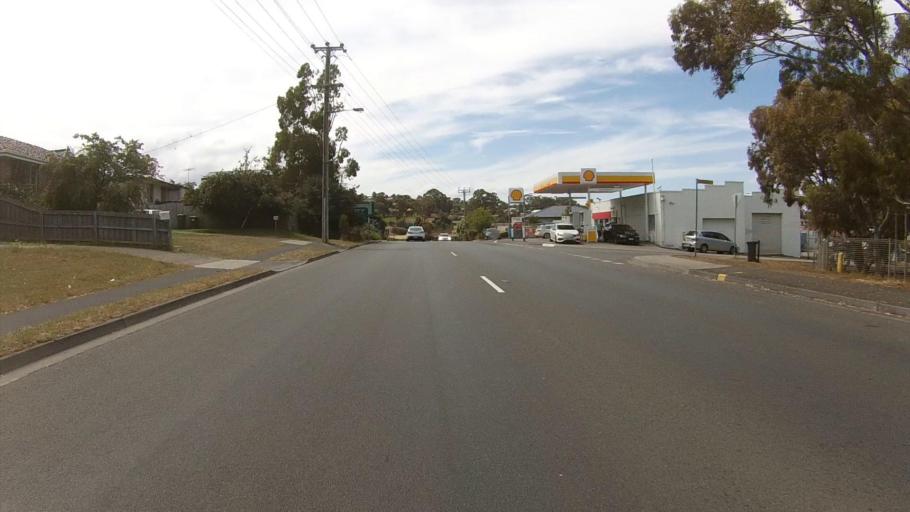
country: AU
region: Tasmania
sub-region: Kingborough
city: Blackmans Bay
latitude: -43.0006
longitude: 147.3202
